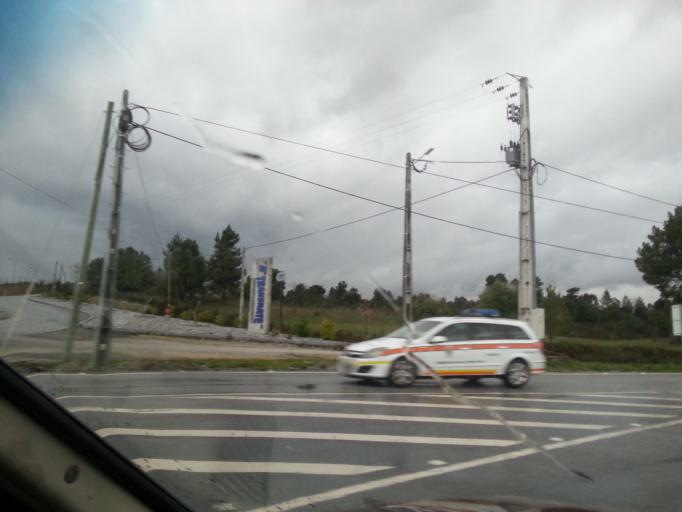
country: PT
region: Guarda
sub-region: Celorico da Beira
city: Celorico da Beira
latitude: 40.6366
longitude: -7.3519
